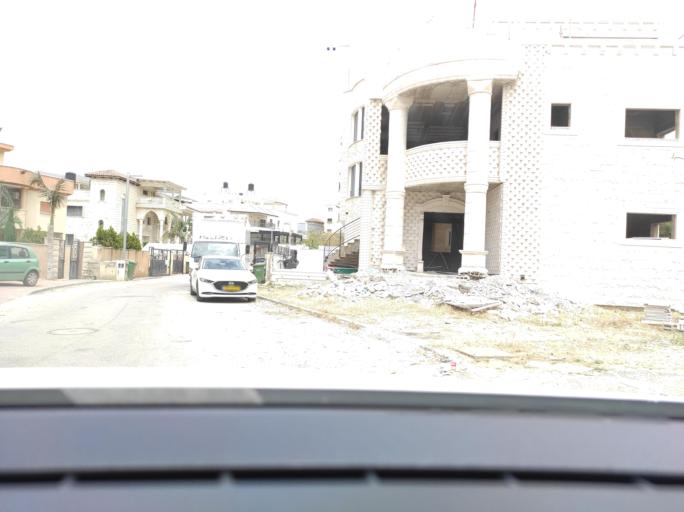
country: IL
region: Central District
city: Kafr Qasim
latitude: 32.1156
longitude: 34.9651
